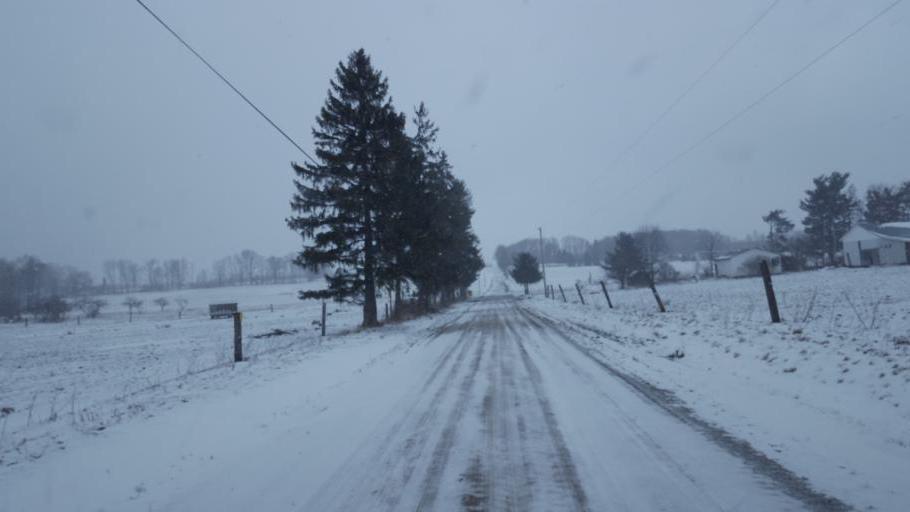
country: US
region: Pennsylvania
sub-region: Crawford County
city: Cochranton
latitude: 41.4352
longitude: -80.0907
